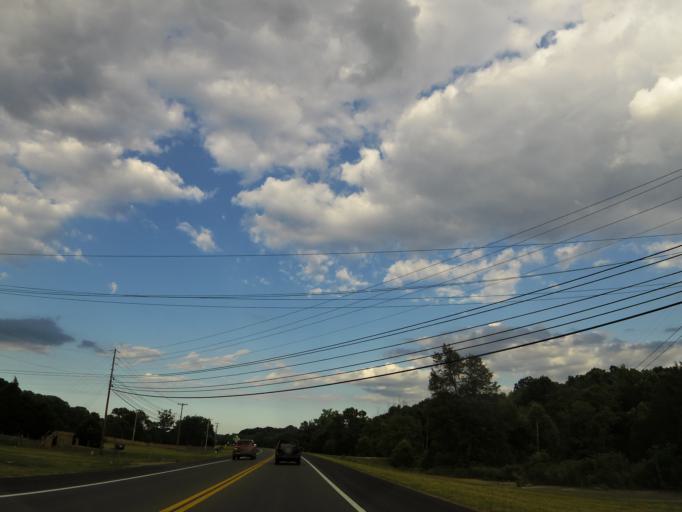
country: US
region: Tennessee
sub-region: Maury County
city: Columbia
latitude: 35.6361
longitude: -86.9894
